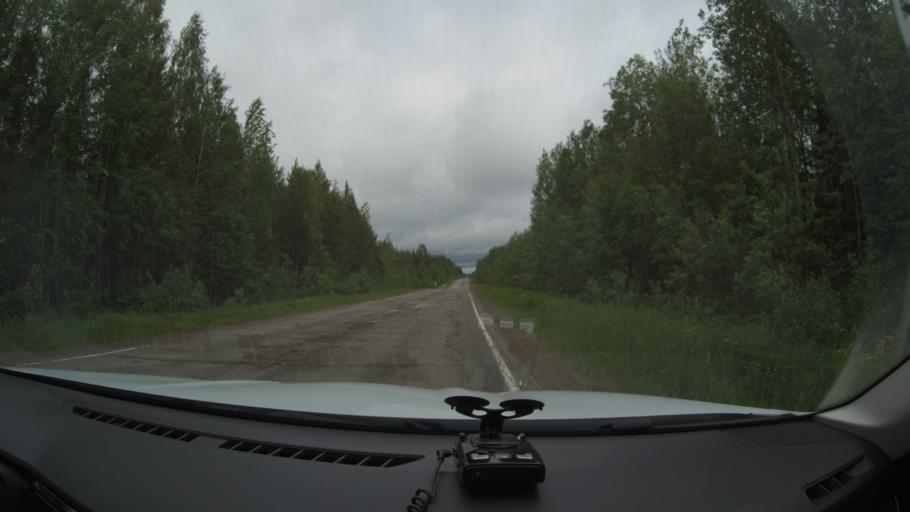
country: RU
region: Komi Republic
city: Nizhniy Odes
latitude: 63.6547
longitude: 54.6692
